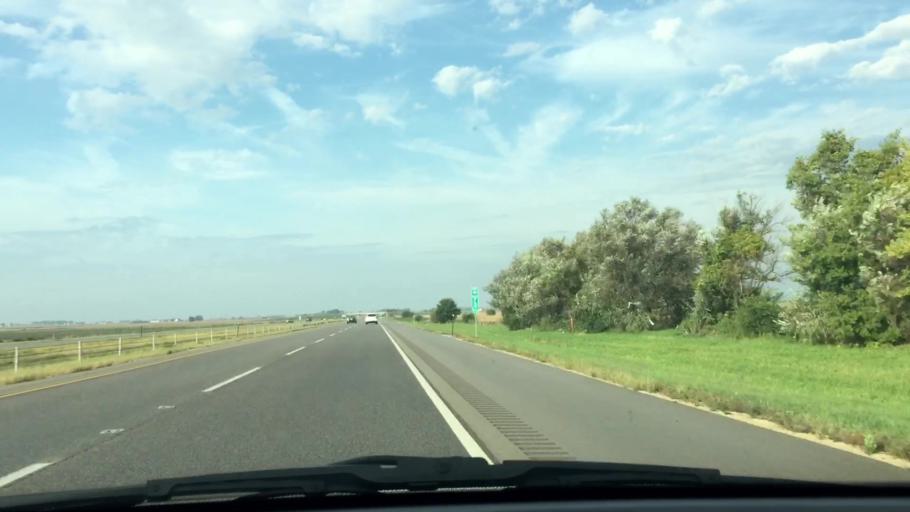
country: US
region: Illinois
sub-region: Ogle County
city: Rochelle
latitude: 41.8858
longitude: -89.1144
